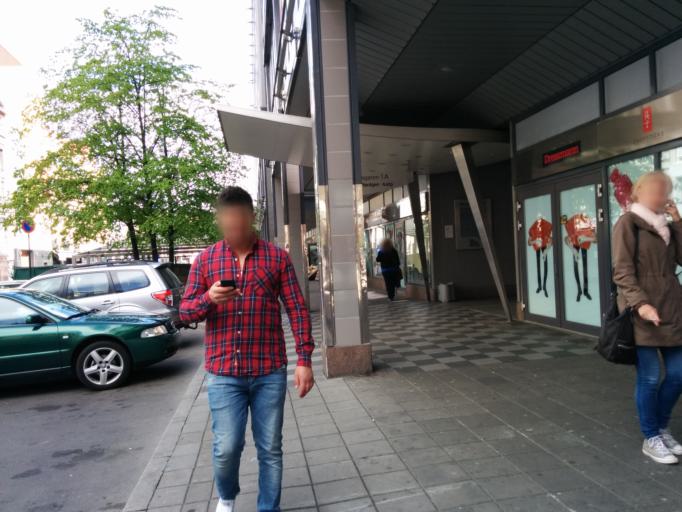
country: NO
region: Oslo
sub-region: Oslo
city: Oslo
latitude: 59.9129
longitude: 10.7514
